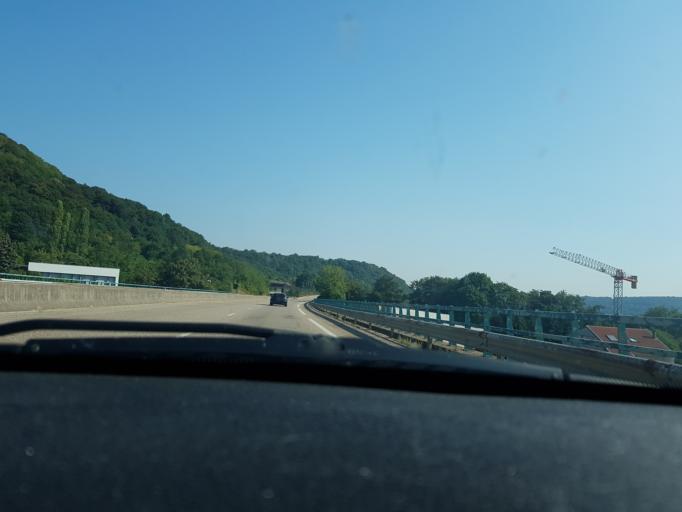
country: FR
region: Lorraine
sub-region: Departement de Meurthe-et-Moselle
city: Maxeville
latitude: 48.7124
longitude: 6.1615
